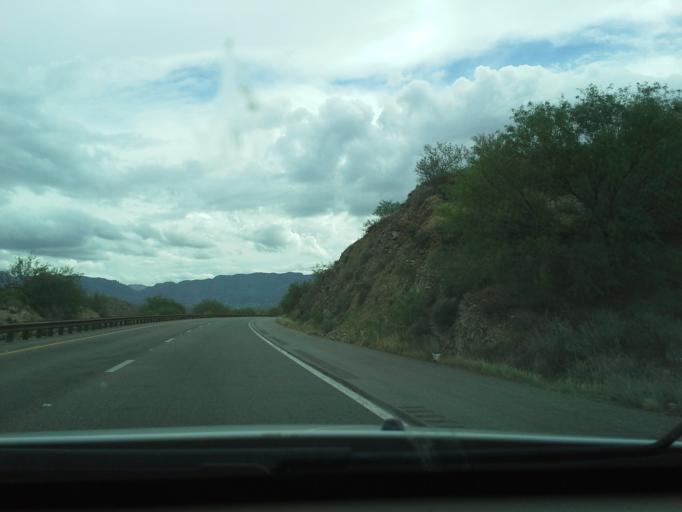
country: US
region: Arizona
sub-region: Pinal County
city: Gold Camp
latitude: 33.2745
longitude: -111.2038
